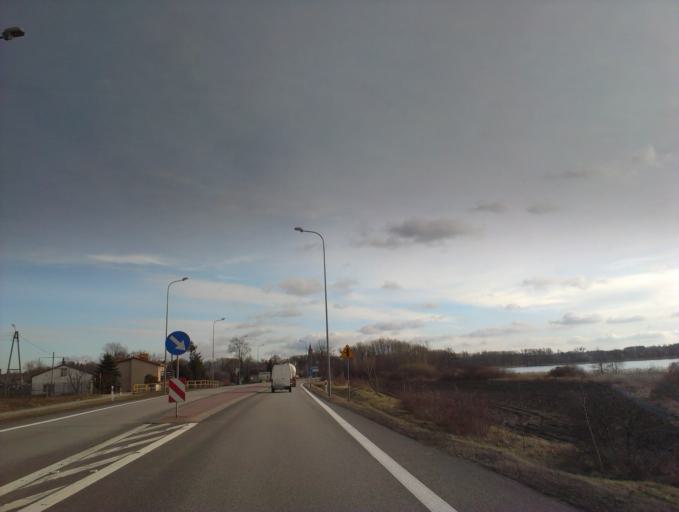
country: PL
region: Kujawsko-Pomorskie
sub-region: Powiat lipnowski
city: Kikol
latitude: 52.9146
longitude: 19.1111
